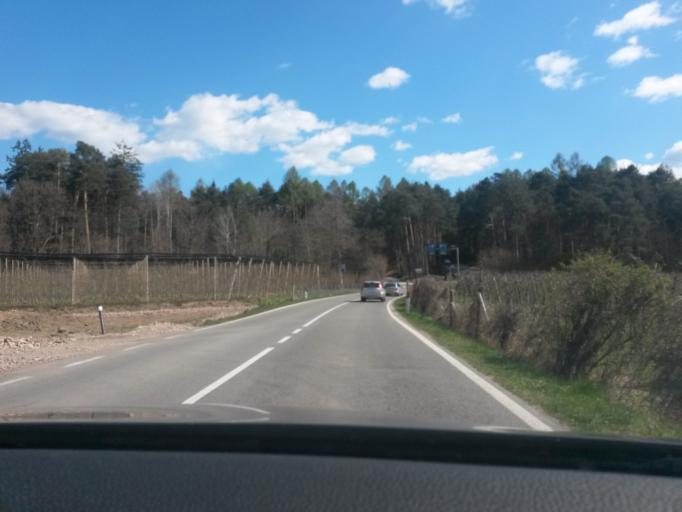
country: IT
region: Trentino-Alto Adige
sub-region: Bolzano
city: Cornaiano
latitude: 46.4400
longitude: 11.2820
